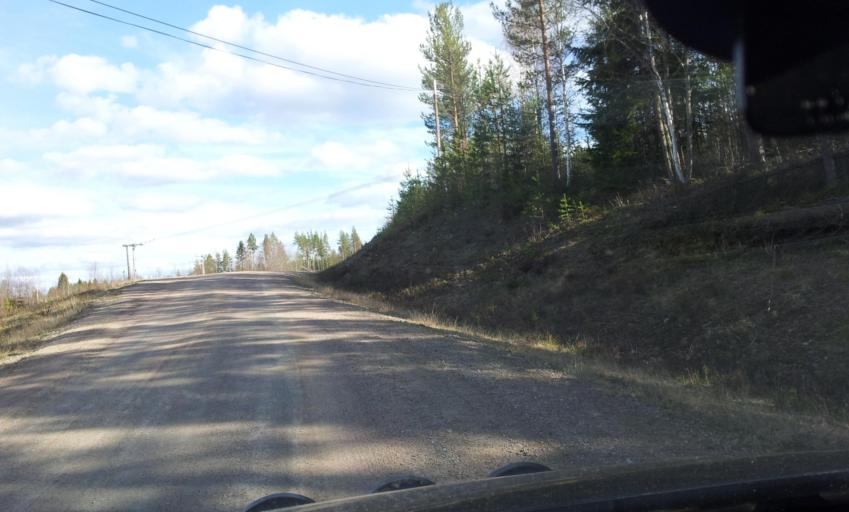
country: SE
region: Vaesternorrland
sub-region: Ange Kommun
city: Ange
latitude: 62.1776
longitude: 15.6328
